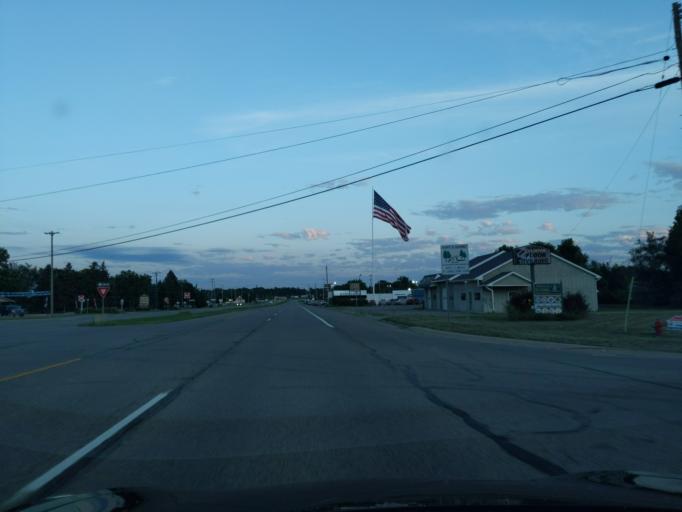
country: US
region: Michigan
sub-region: Clinton County
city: Saint Johns
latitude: 43.0162
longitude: -84.5607
